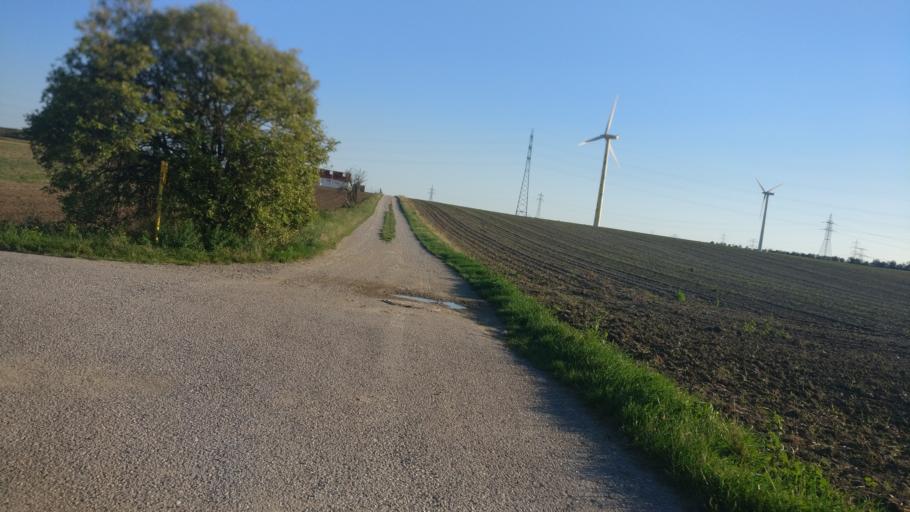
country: AT
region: Lower Austria
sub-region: Politischer Bezirk Wien-Umgebung
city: Lanzendorf
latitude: 48.1305
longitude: 16.4341
